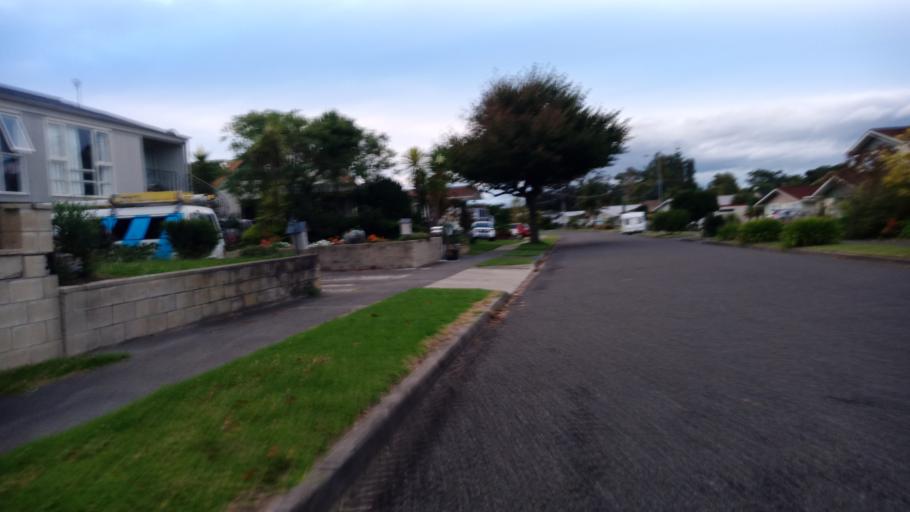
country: NZ
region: Gisborne
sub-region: Gisborne District
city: Gisborne
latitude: -38.6498
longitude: 178.0085
